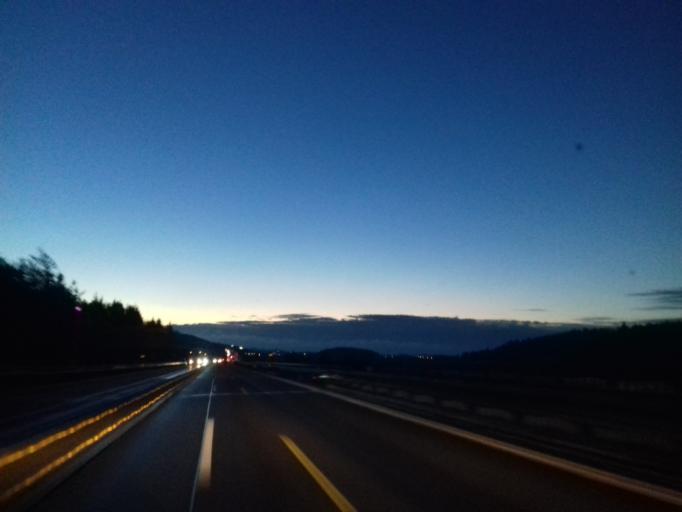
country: CZ
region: Vysocina
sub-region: Okres Zd'ar nad Sazavou
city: Velke Mezirici
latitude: 49.3737
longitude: 15.9616
